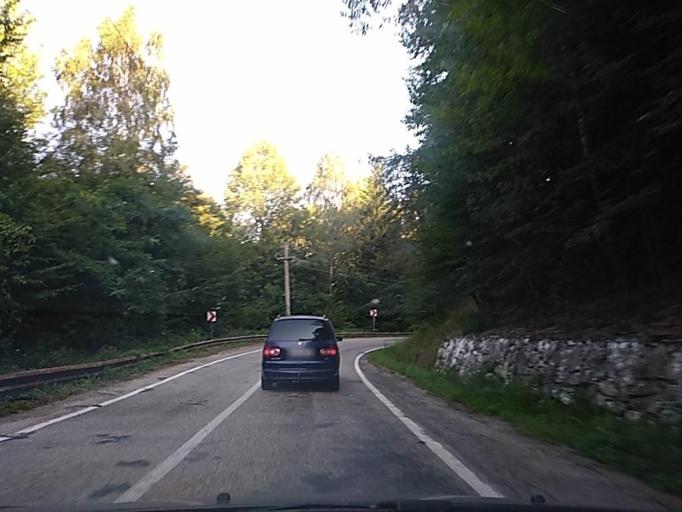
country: RO
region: Arges
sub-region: Comuna Arefu
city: Arefu
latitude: 45.3774
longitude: 24.6346
